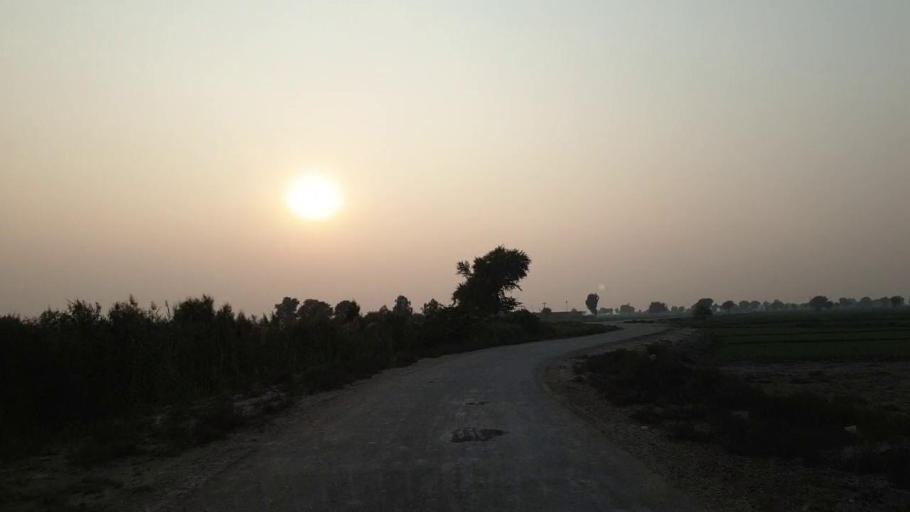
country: PK
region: Sindh
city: Bhan
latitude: 26.5306
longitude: 67.7008
